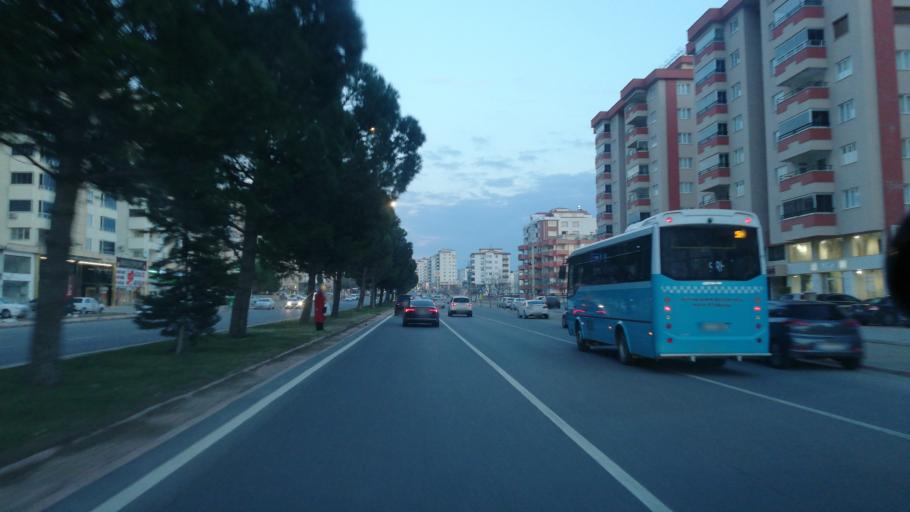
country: TR
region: Kahramanmaras
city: Kahramanmaras
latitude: 37.5953
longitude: 36.8524
